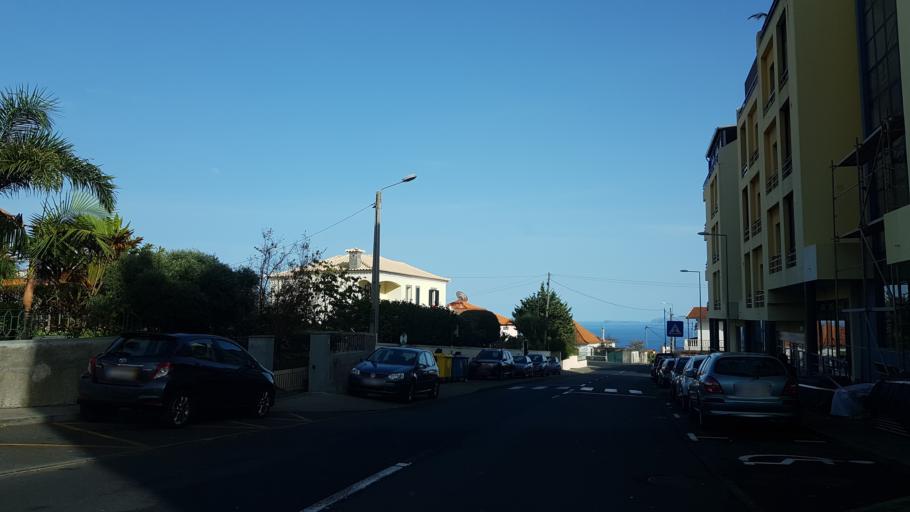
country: PT
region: Madeira
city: Canico
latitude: 32.6478
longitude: -16.8452
